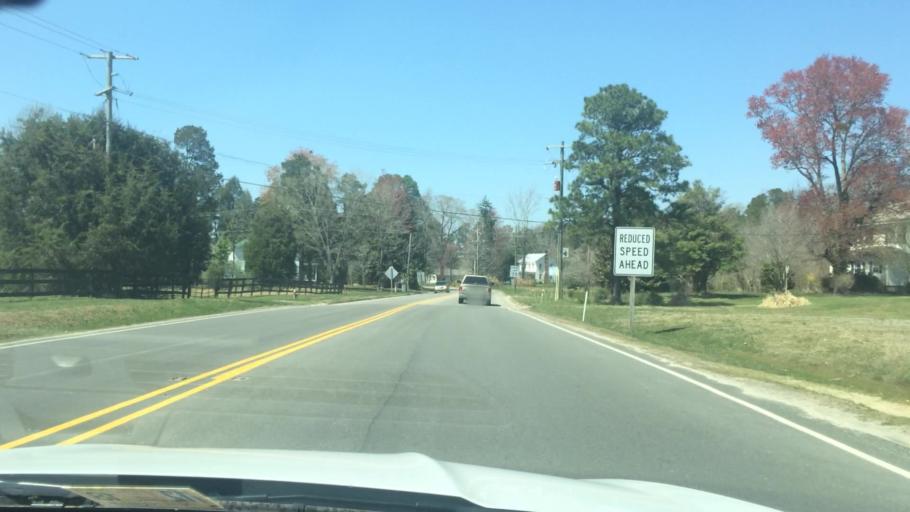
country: US
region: Virginia
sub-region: Middlesex County
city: Saluda
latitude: 37.6031
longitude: -76.5881
